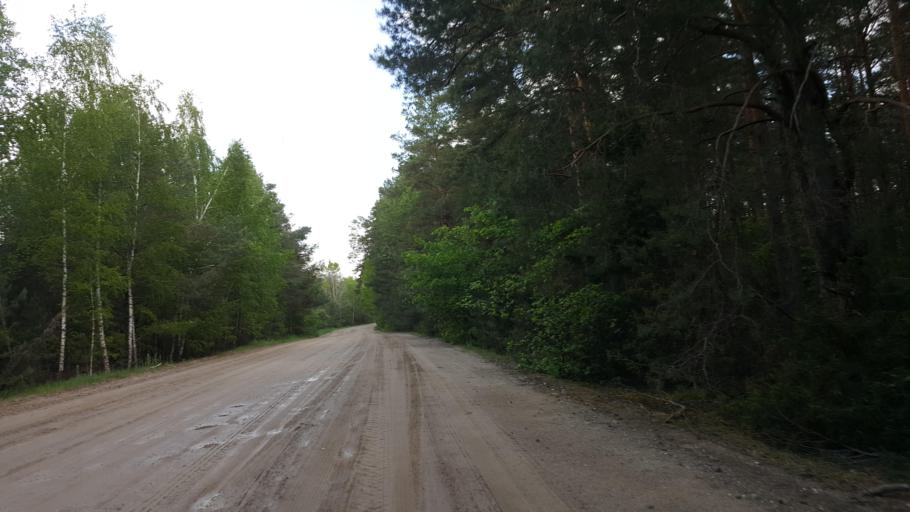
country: BY
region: Brest
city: Kamyanyets
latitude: 52.4374
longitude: 23.9733
